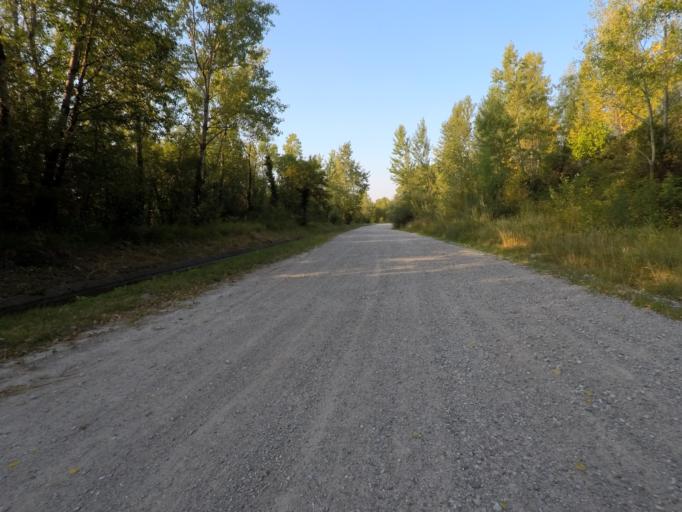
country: IT
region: Friuli Venezia Giulia
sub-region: Provincia di Udine
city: Gemona
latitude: 46.2860
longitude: 13.1009
